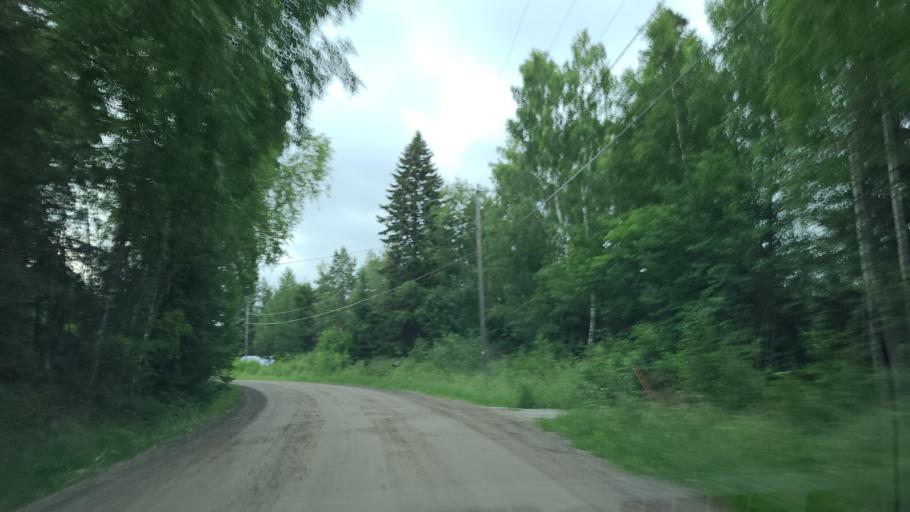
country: FI
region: Ostrobothnia
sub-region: Vaasa
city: Replot
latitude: 63.3086
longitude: 21.1578
